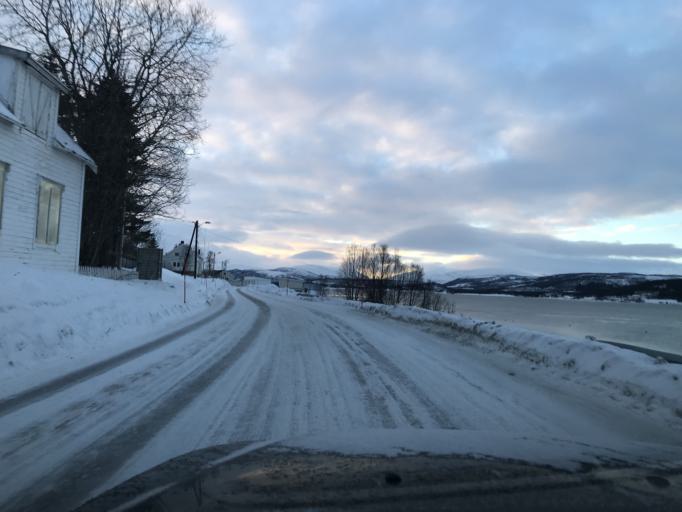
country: NO
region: Troms
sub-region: Lenvik
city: Finnsnes
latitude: 69.3423
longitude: 18.0964
